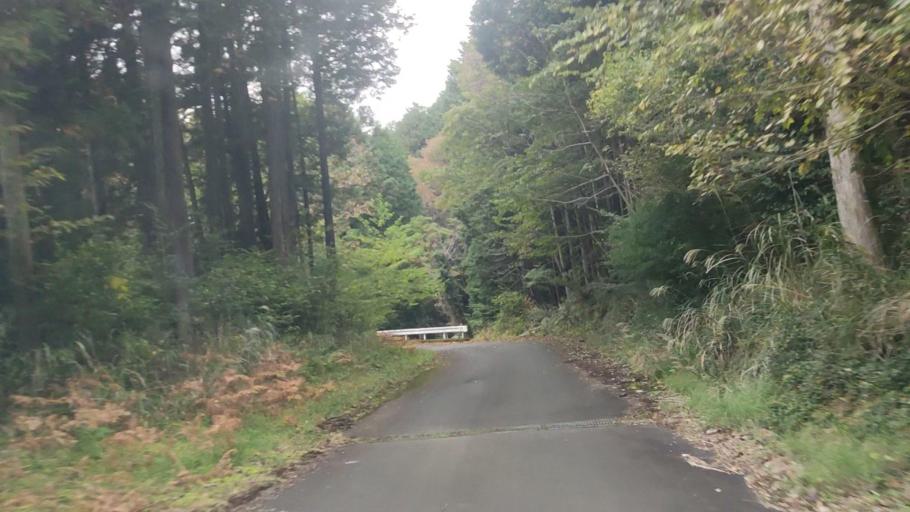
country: JP
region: Shizuoka
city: Ito
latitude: 34.9213
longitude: 138.9839
